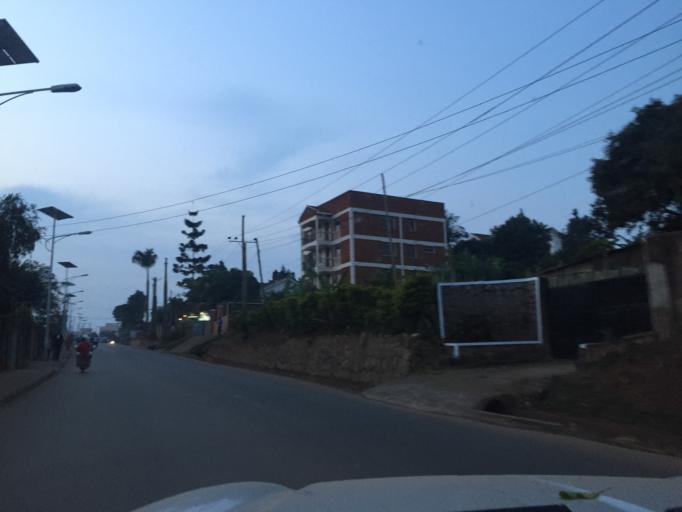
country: UG
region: Central Region
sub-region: Kampala District
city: Kampala
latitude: 0.2990
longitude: 32.6034
